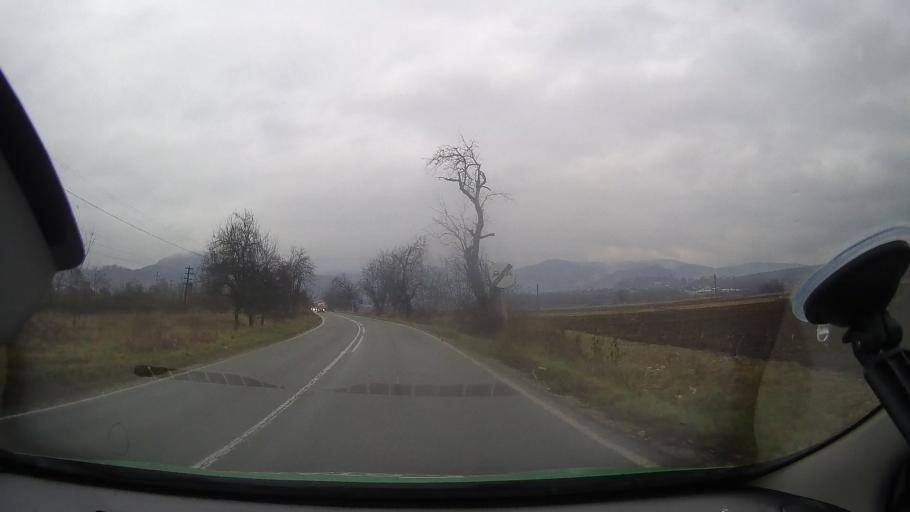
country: RO
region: Arad
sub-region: Comuna Gurahont
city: Gurahont
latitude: 46.2744
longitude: 22.3292
